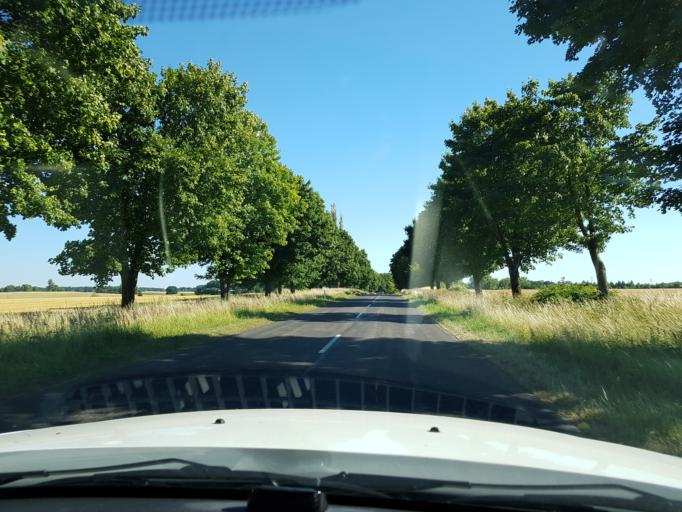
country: PL
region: West Pomeranian Voivodeship
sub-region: Powiat lobeski
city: Lobez
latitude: 53.6900
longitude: 15.6073
